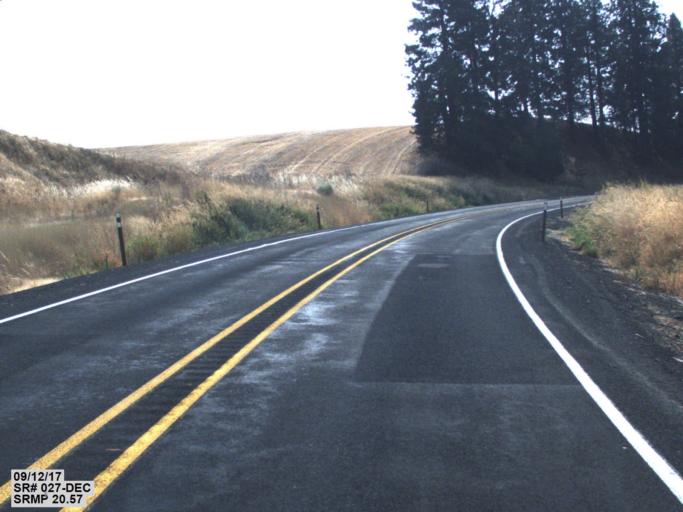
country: US
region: Washington
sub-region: Whitman County
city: Pullman
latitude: 46.9664
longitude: -117.1099
